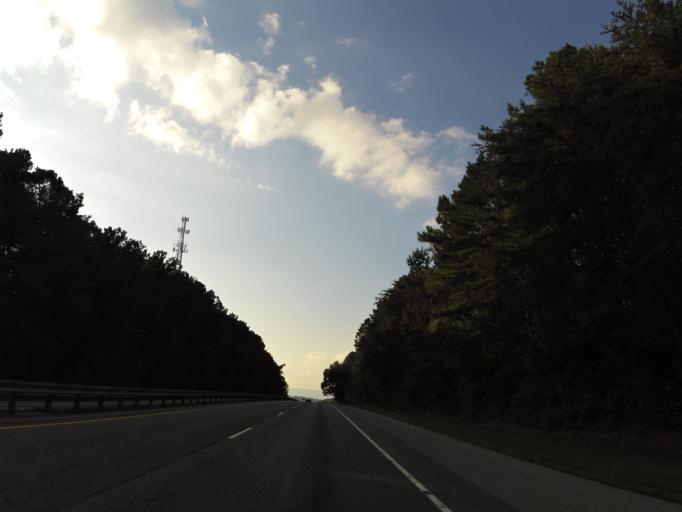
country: US
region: Tennessee
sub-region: Knox County
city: Farragut
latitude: 35.9718
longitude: -84.1772
